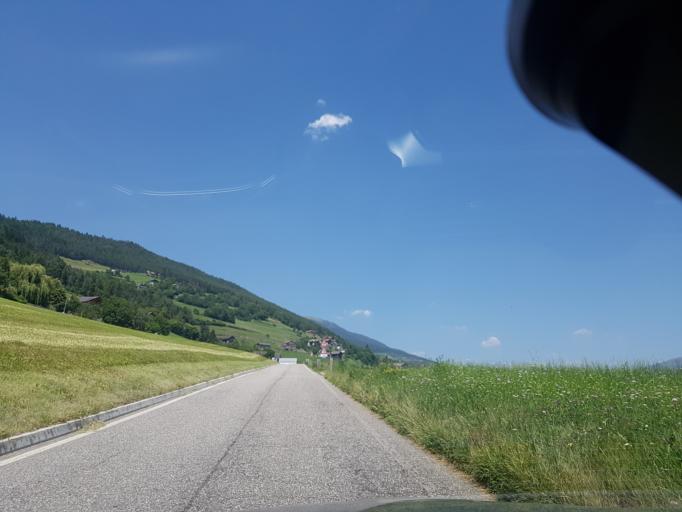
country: IT
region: Trentino-Alto Adige
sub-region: Bolzano
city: Villandro
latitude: 46.6329
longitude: 11.5381
